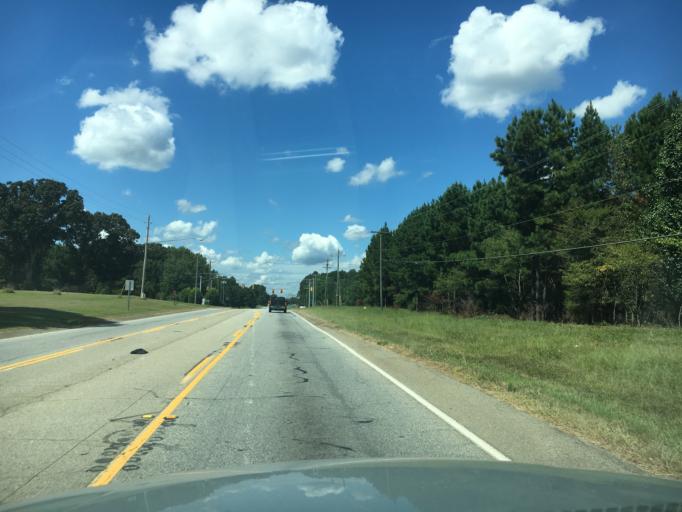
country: US
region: South Carolina
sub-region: Laurens County
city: Laurens
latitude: 34.5012
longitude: -82.0573
